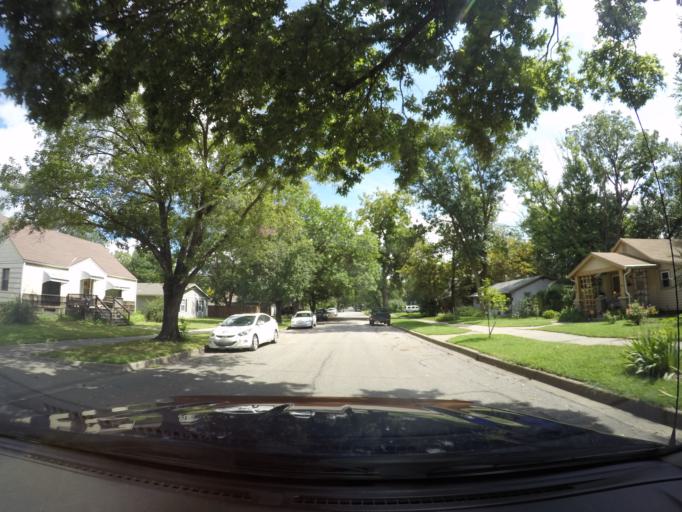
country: US
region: Kansas
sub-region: Riley County
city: Manhattan
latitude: 39.1764
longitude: -96.5779
